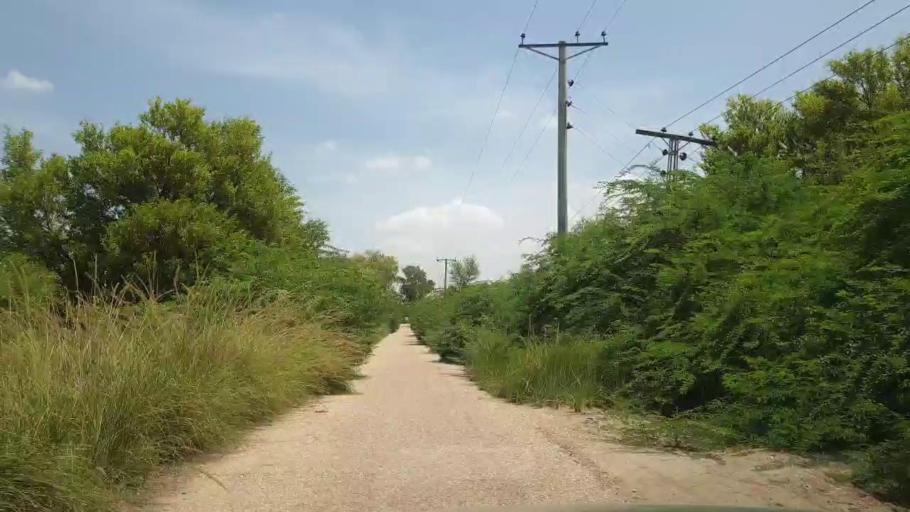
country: PK
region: Sindh
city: Kot Diji
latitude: 27.1365
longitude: 69.0082
